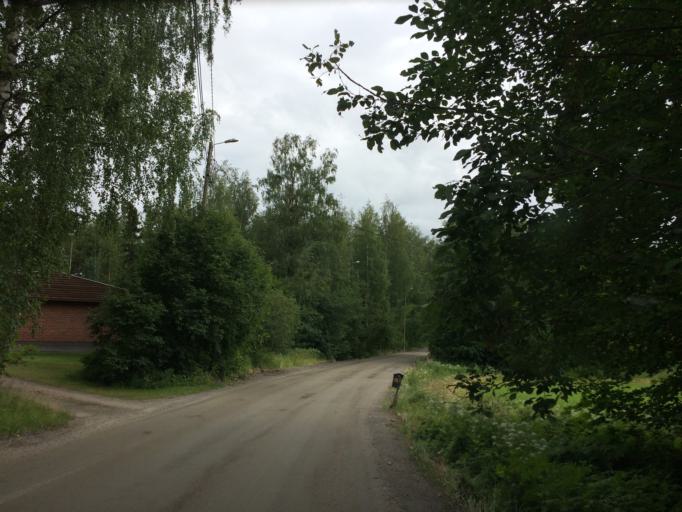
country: FI
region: Haeme
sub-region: Haemeenlinna
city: Haemeenlinna
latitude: 60.9721
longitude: 24.5207
